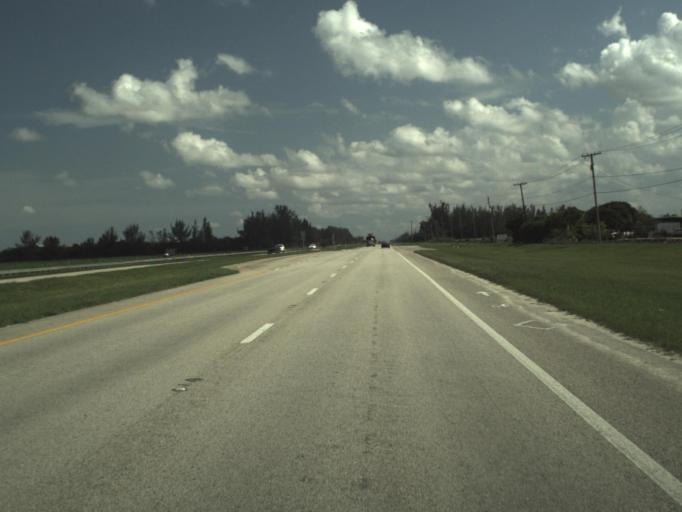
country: US
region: Florida
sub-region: Palm Beach County
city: Villages of Oriole
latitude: 26.4897
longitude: -80.2051
